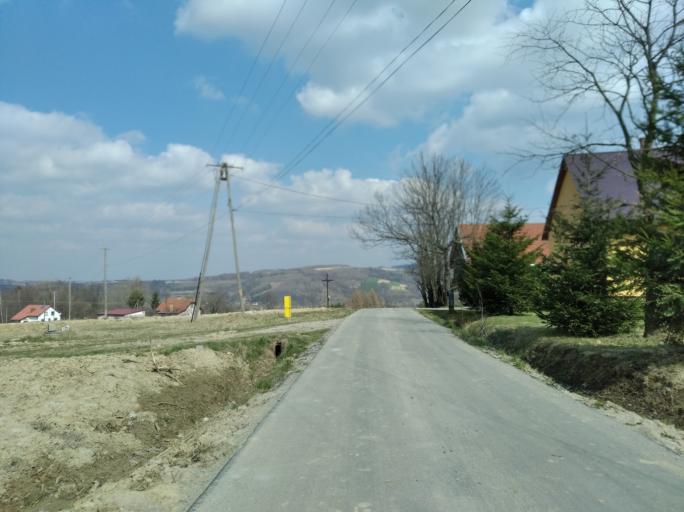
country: PL
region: Subcarpathian Voivodeship
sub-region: Powiat strzyzowski
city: Strzyzow
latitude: 49.8345
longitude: 21.8072
